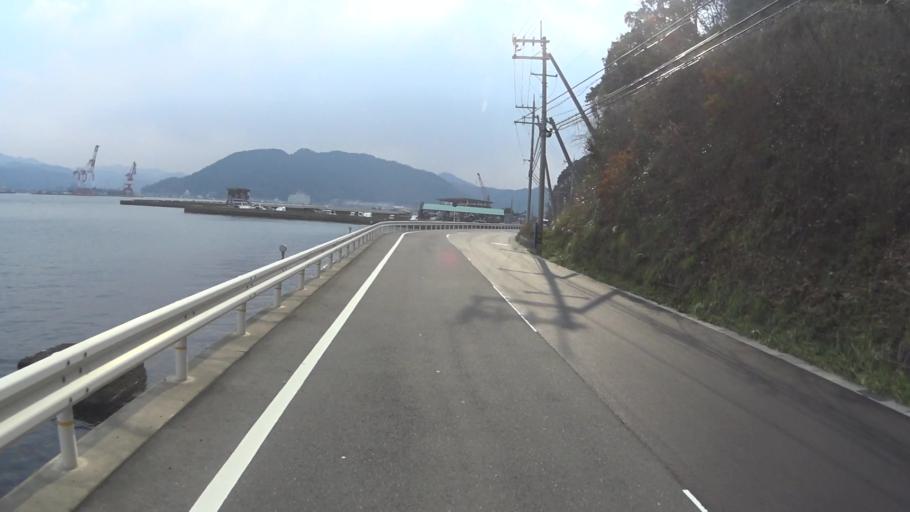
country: JP
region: Kyoto
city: Maizuru
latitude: 35.4653
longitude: 135.3170
